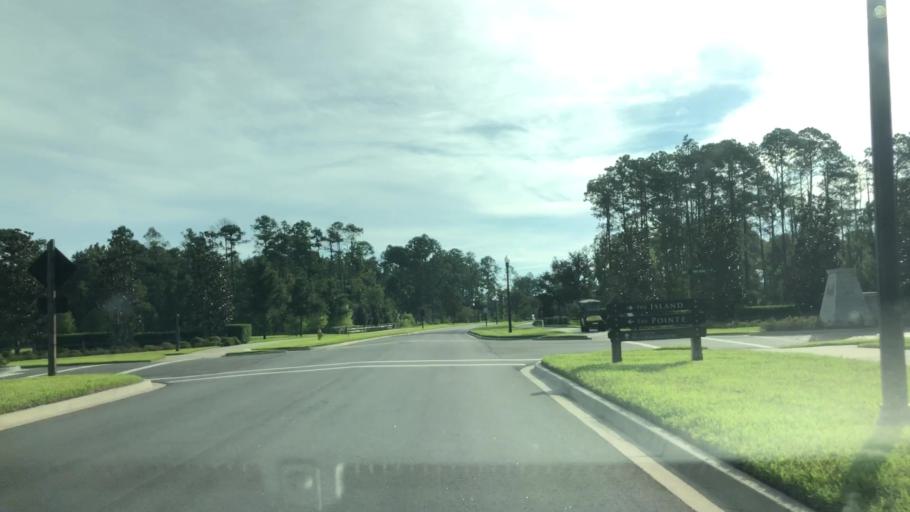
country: US
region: Florida
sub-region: Saint Johns County
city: Palm Valley
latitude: 30.1299
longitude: -81.4157
